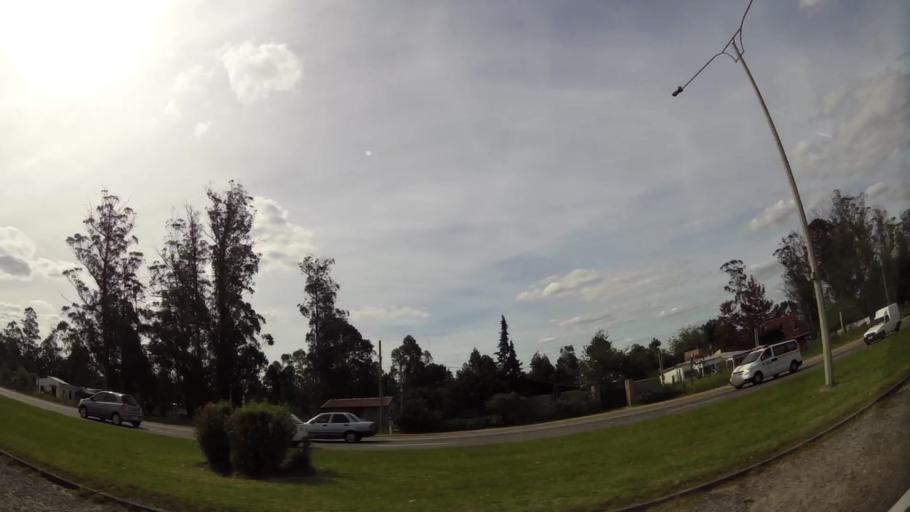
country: UY
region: Canelones
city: Empalme Olmos
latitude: -34.7811
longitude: -55.8755
